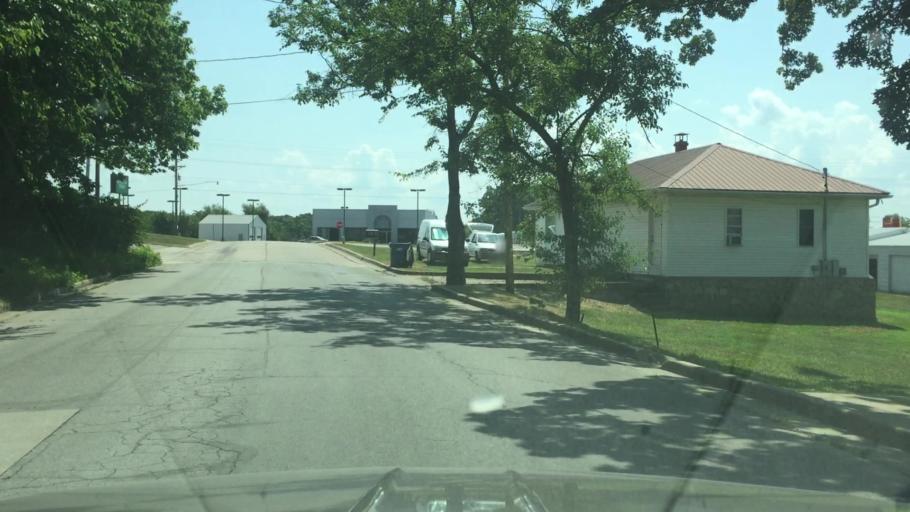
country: US
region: Missouri
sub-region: Miller County
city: Eldon
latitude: 38.3371
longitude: -92.5860
